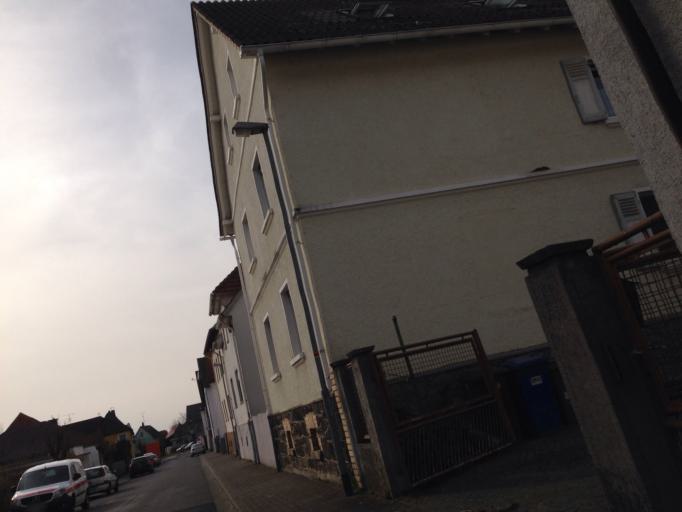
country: DE
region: Hesse
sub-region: Regierungsbezirk Giessen
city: Grossen Buseck
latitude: 50.6088
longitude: 8.7908
